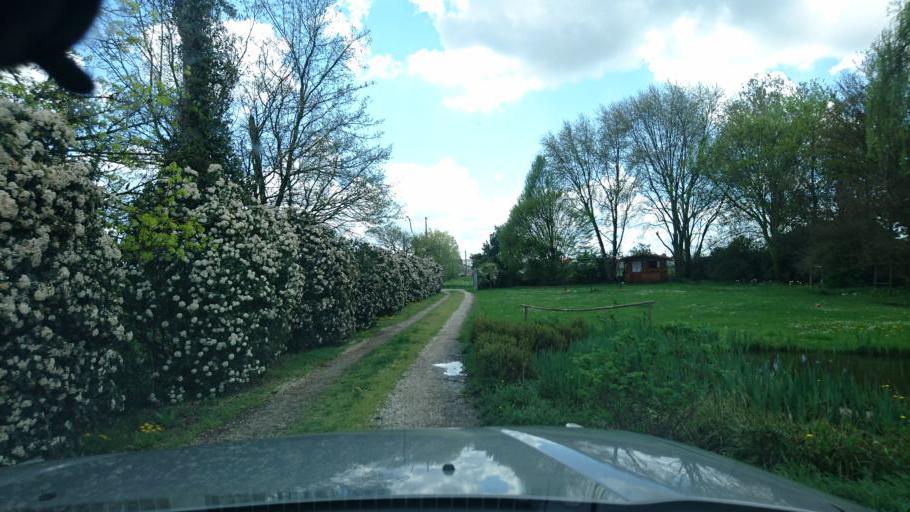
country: IT
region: Veneto
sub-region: Provincia di Padova
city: Piazzola sul Brenta
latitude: 45.5464
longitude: 11.7649
